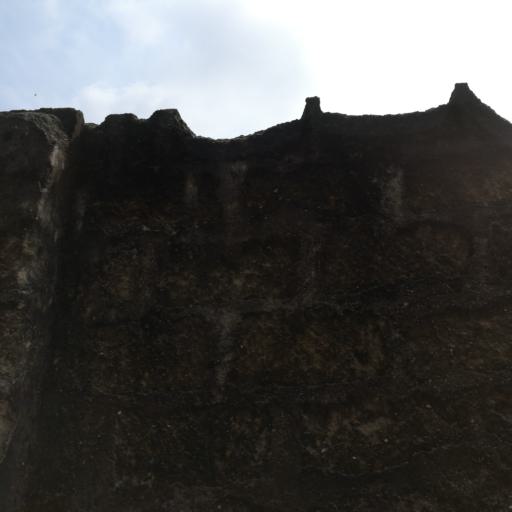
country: NG
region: Rivers
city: Port Harcourt
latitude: 4.8344
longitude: 7.0655
